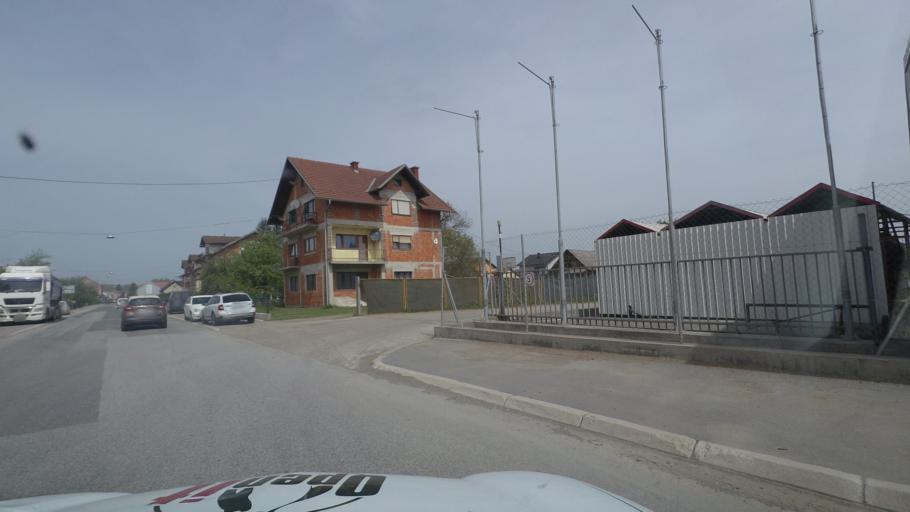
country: HR
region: Sisacko-Moslavacka
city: Glina
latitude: 45.3340
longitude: 16.0971
